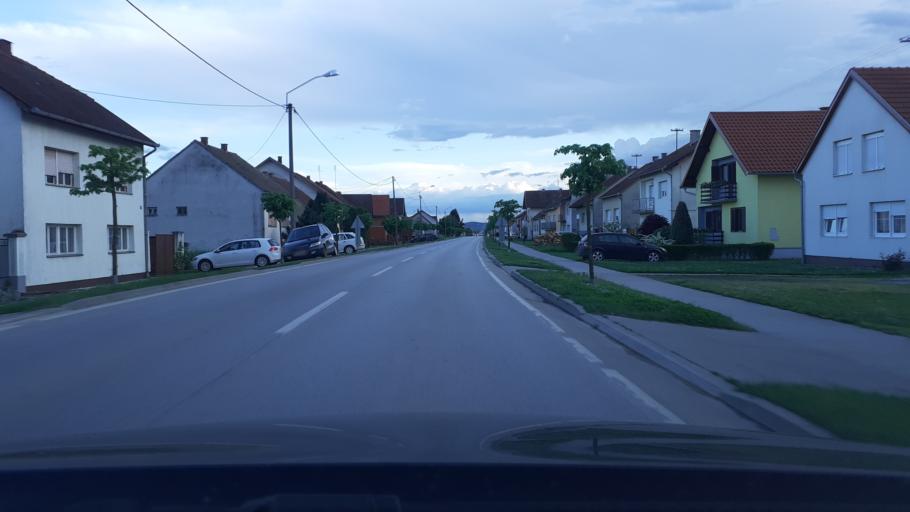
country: HR
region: Pozesko-Slavonska
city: Pleternica
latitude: 45.2955
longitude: 17.8081
